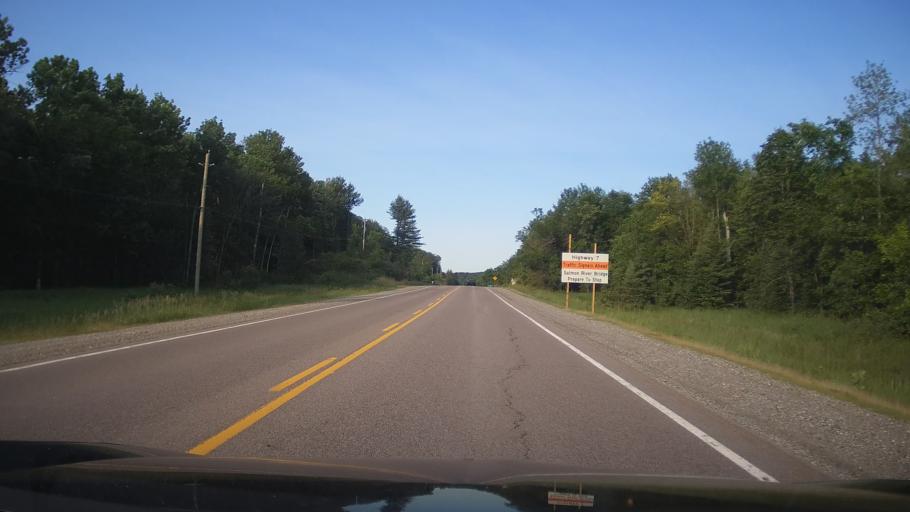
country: CA
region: Ontario
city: Skatepark
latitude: 44.7502
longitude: -76.9146
